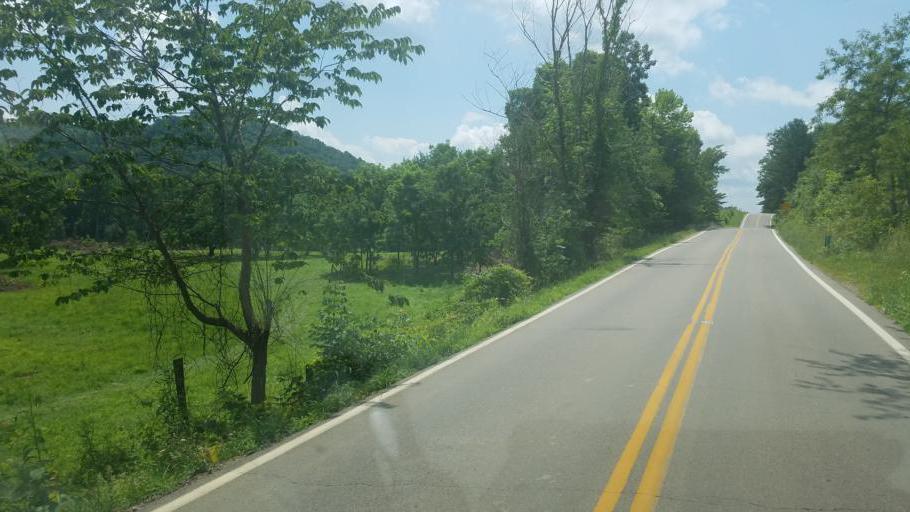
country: US
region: Ohio
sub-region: Ross County
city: Kingston
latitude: 39.3495
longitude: -82.7237
